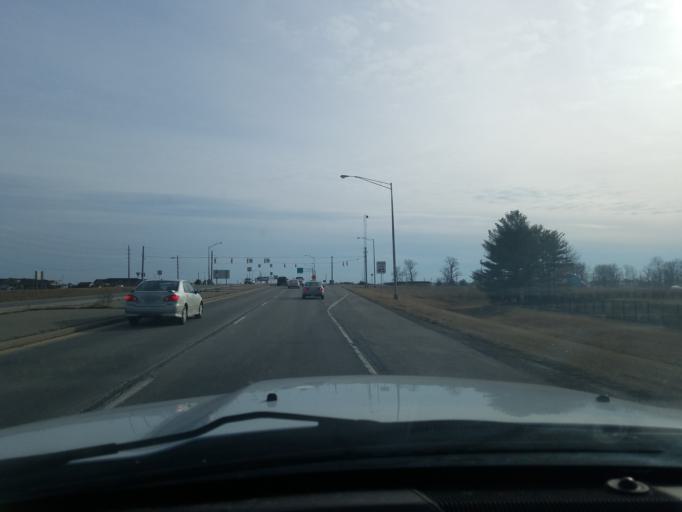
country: US
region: Indiana
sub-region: Hancock County
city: Greenfield
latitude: 39.8234
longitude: -85.7701
